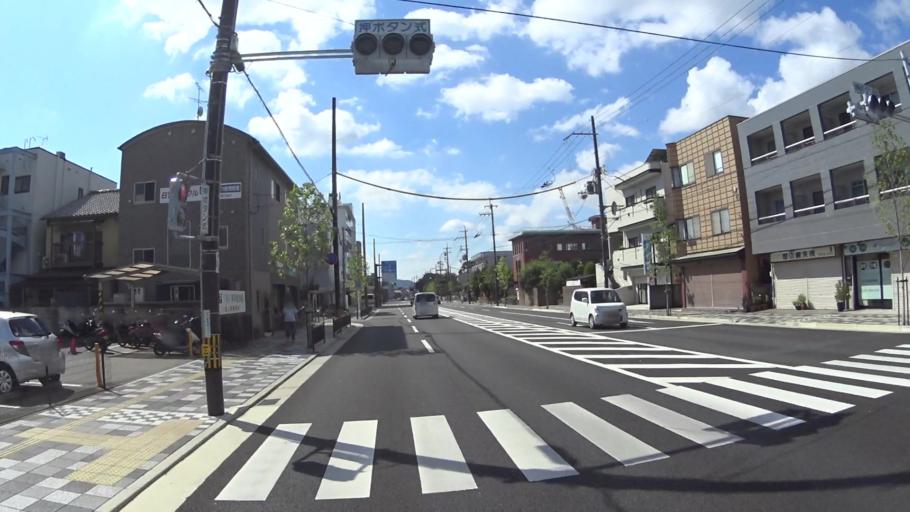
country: JP
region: Kyoto
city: Muko
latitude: 34.9252
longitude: 135.6993
